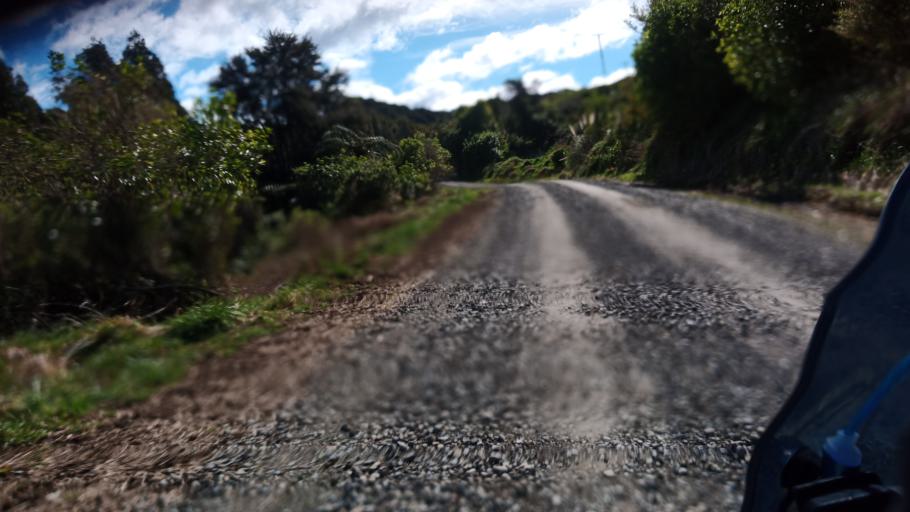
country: NZ
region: Hawke's Bay
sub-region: Wairoa District
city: Wairoa
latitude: -38.8204
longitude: 177.1617
